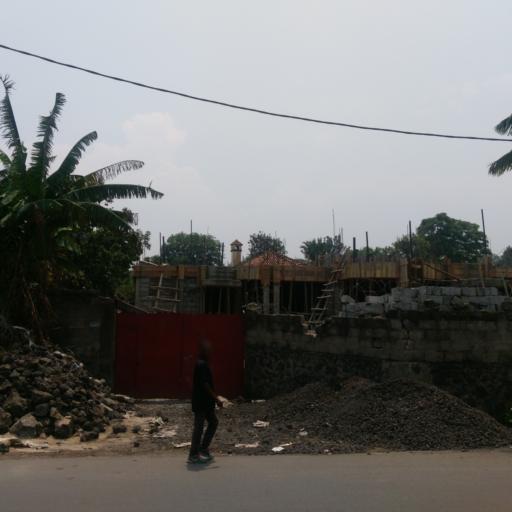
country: RW
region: Western Province
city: Gisenyi
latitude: -1.6986
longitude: 29.2382
